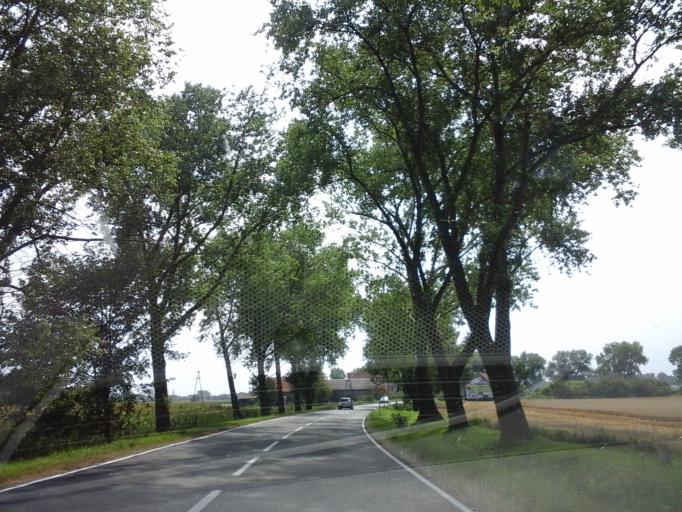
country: PL
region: Lower Silesian Voivodeship
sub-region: Powiat strzelinski
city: Strzelin
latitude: 50.8421
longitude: 17.0589
